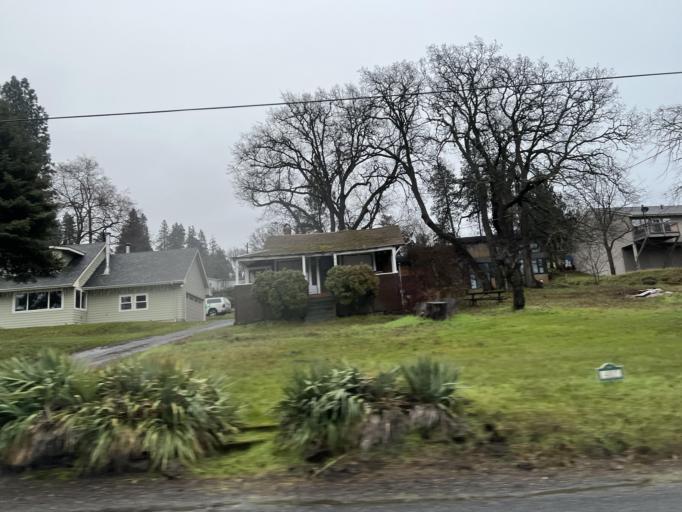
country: US
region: Washington
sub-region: Klickitat County
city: White Salmon
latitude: 45.6857
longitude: -121.3921
